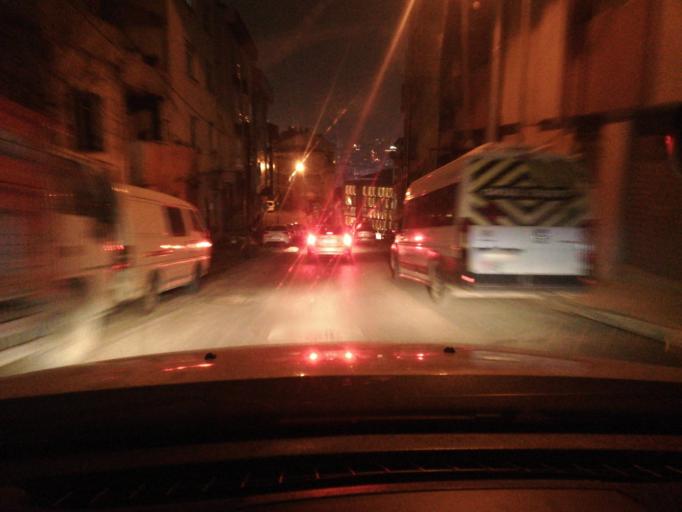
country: TR
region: Istanbul
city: Sisli
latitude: 41.0760
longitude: 28.9760
